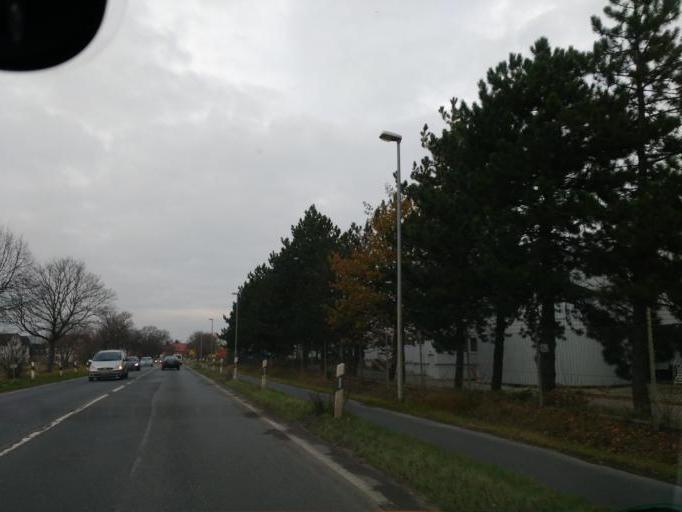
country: DE
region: Lower Saxony
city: Laatzen
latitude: 52.3635
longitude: 9.8646
